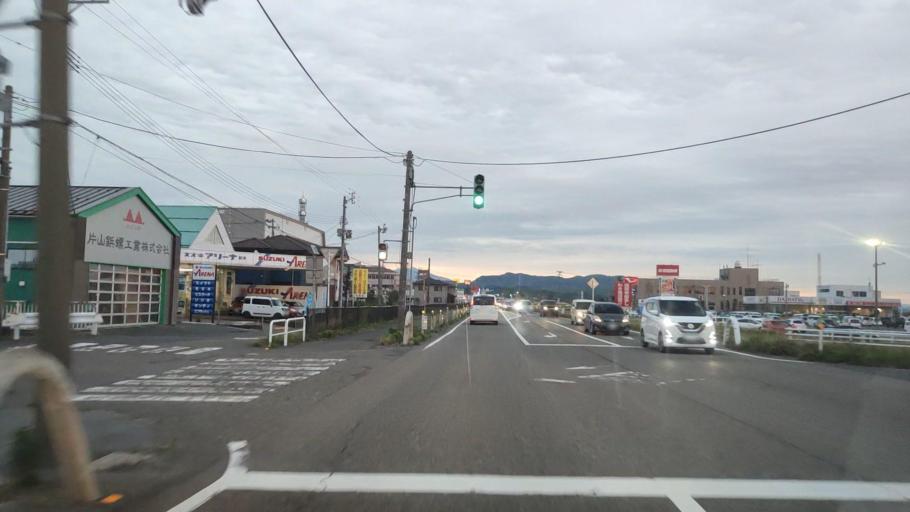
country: JP
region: Niigata
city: Niitsu-honcho
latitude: 37.7899
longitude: 139.1113
